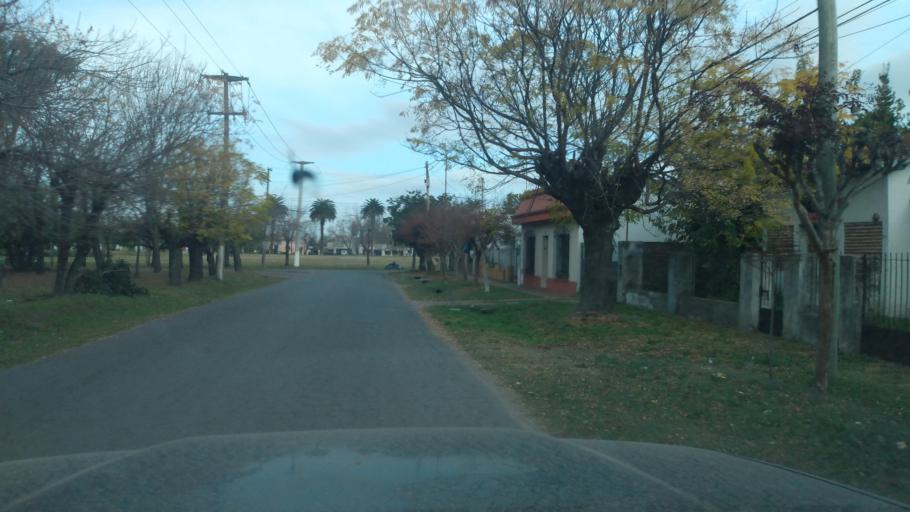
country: AR
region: Buenos Aires
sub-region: Partido de Lujan
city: Lujan
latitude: -34.5991
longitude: -59.1732
